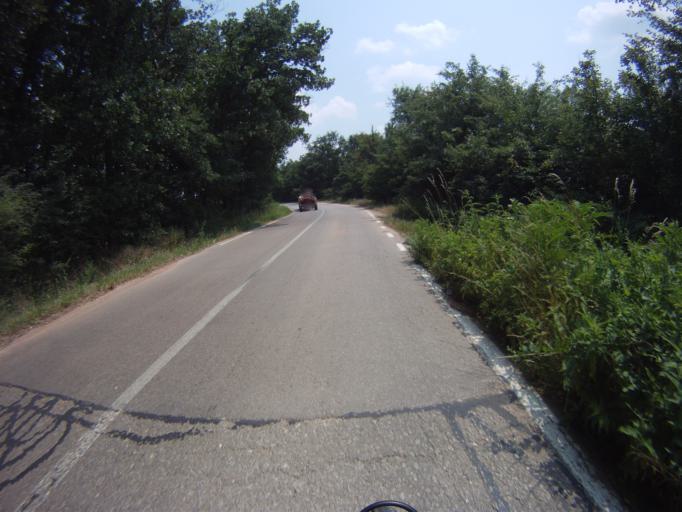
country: RS
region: Central Serbia
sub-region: Nisavski Okrug
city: Gadzin Han
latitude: 43.2025
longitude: 21.9774
